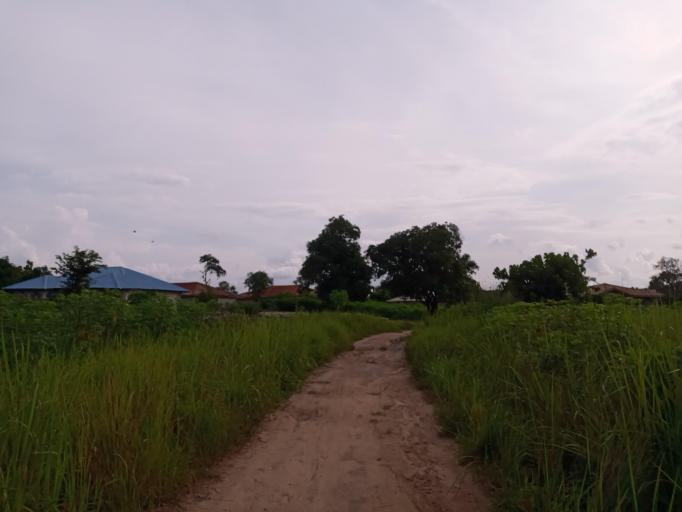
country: SL
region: Northern Province
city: Bumbuna
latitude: 9.0491
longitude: -11.7553
